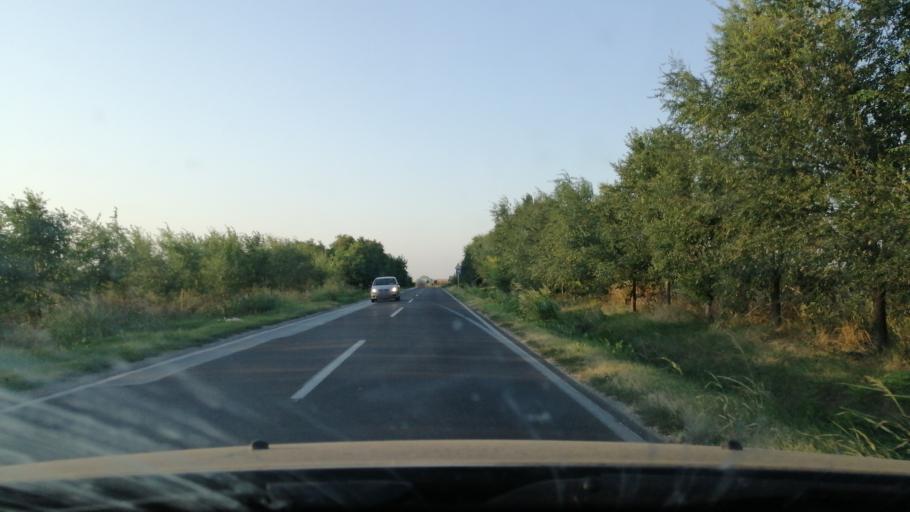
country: RS
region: Central Serbia
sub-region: Belgrade
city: Grocka
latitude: 44.7884
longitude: 20.7237
